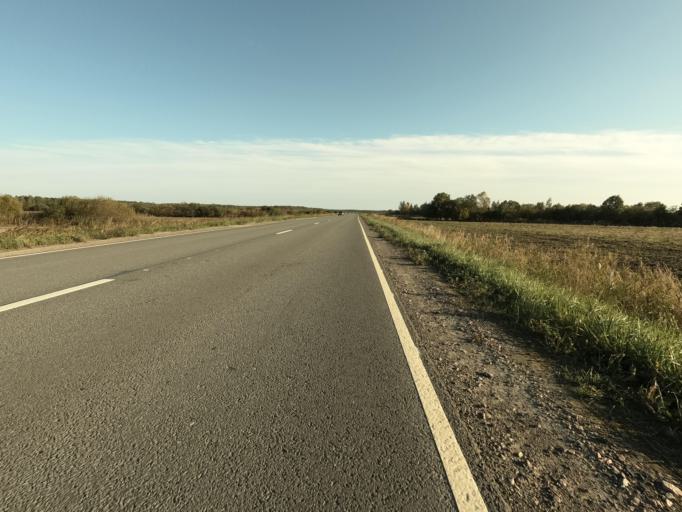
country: RU
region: St.-Petersburg
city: Sapernyy
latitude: 59.7452
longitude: 30.6454
